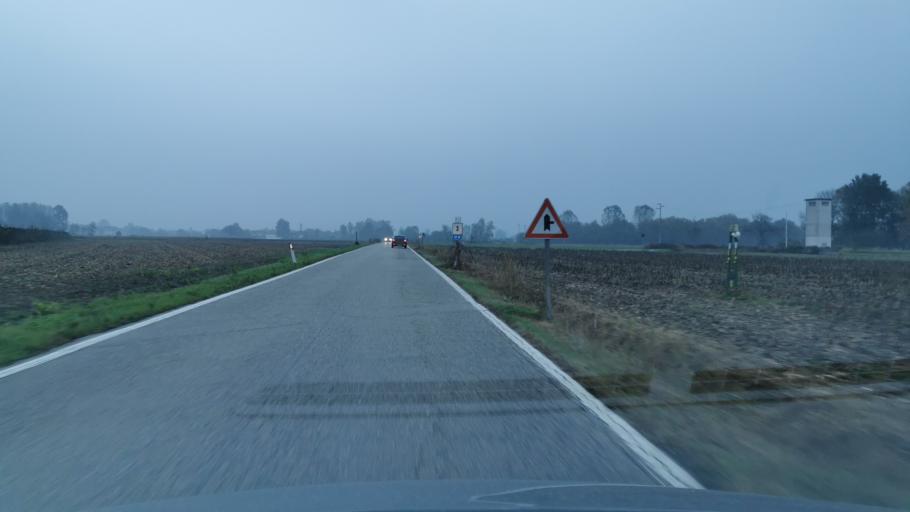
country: IT
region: Piedmont
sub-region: Provincia di Torino
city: Lusiglie
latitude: 45.3193
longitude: 7.7595
